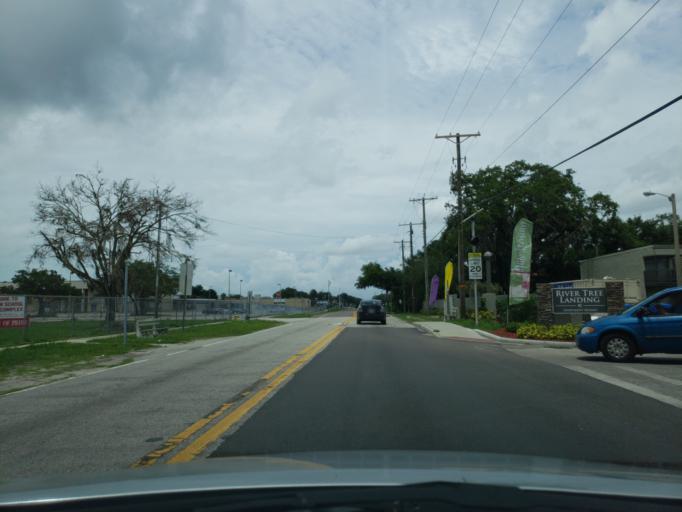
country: US
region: Florida
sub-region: Hillsborough County
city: Temple Terrace
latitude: 28.0107
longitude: -82.3891
